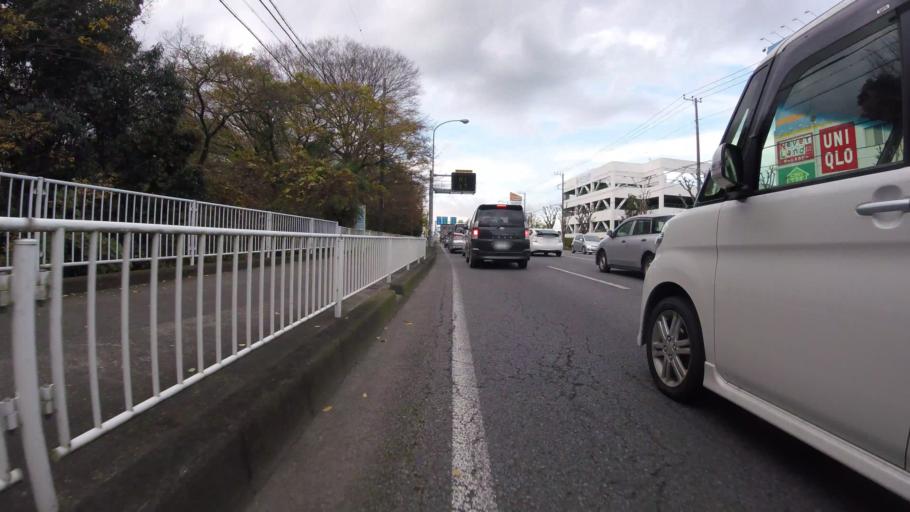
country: JP
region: Shizuoka
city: Mishima
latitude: 35.1081
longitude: 138.9005
